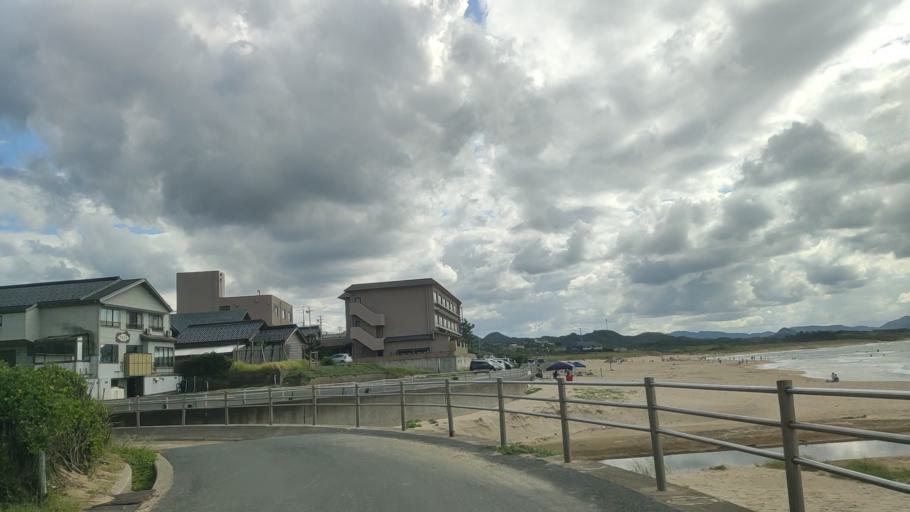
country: JP
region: Hyogo
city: Toyooka
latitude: 35.6669
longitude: 134.9675
